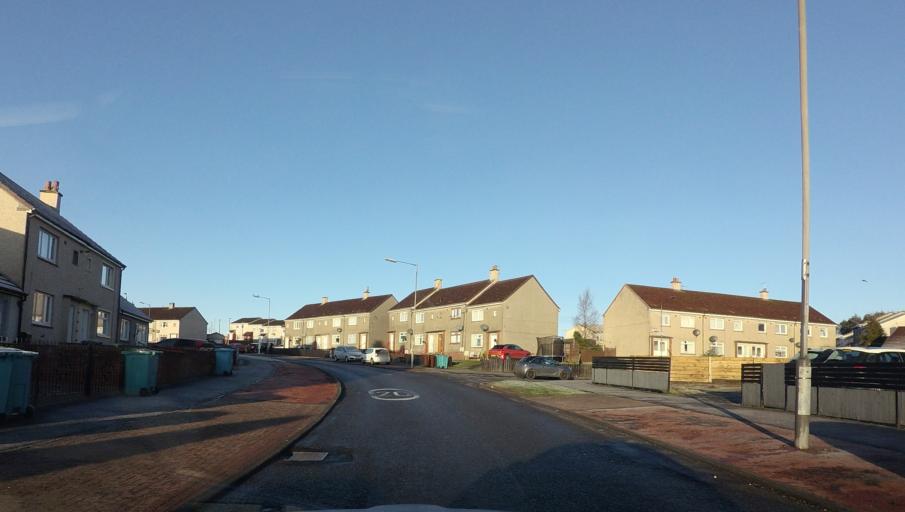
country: GB
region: Scotland
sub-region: North Lanarkshire
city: Shotts
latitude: 55.8250
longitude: -3.7989
